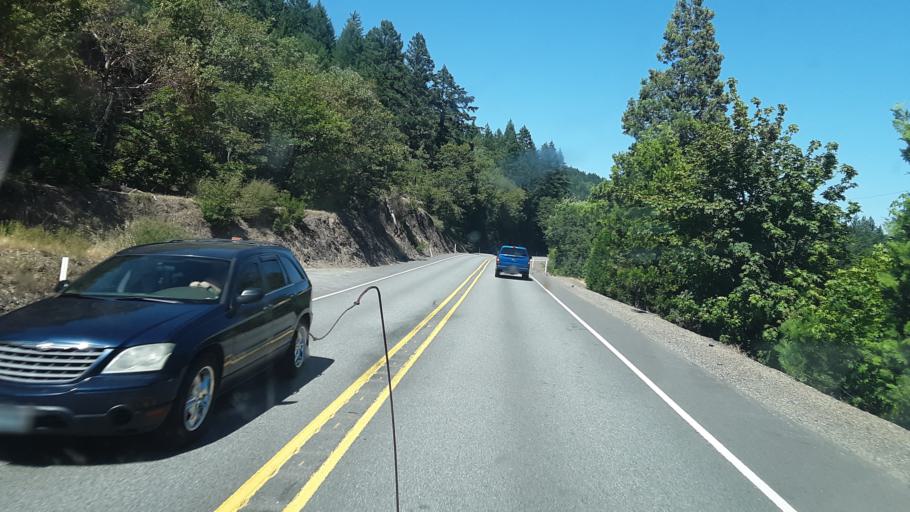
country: US
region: Oregon
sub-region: Josephine County
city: Redwood
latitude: 42.3789
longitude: -123.4931
